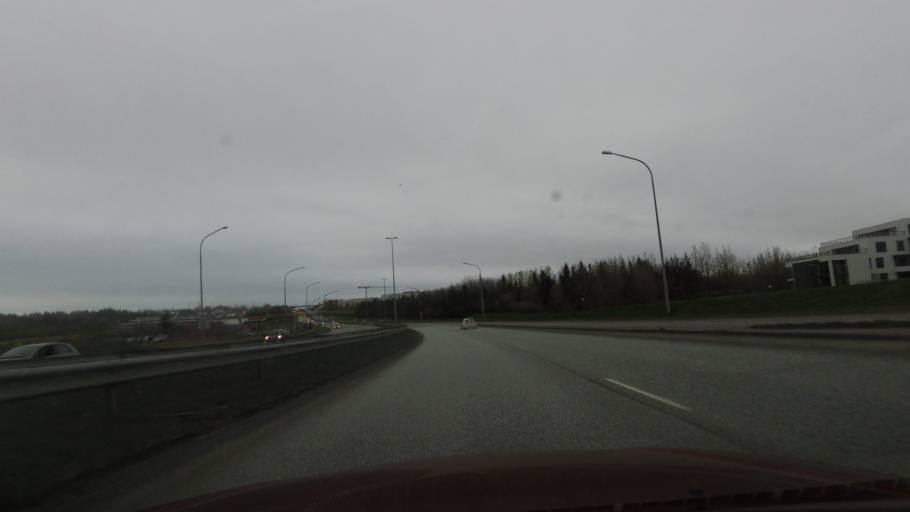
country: IS
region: Capital Region
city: Kopavogur
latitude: 64.1160
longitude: -21.8985
